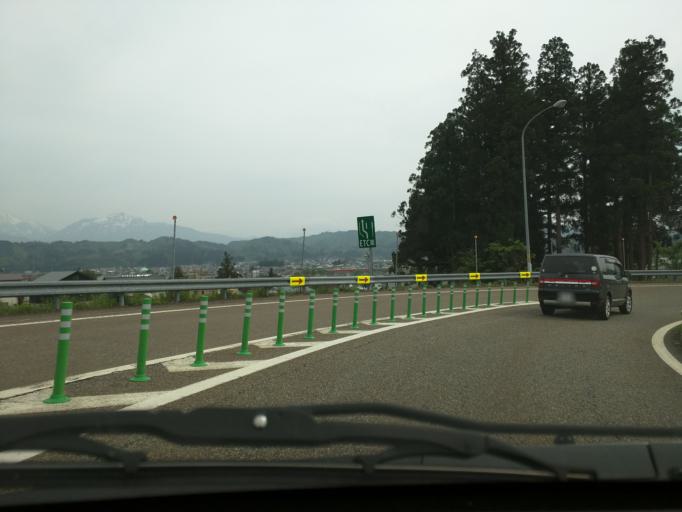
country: JP
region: Niigata
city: Ojiya
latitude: 37.2542
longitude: 138.9267
